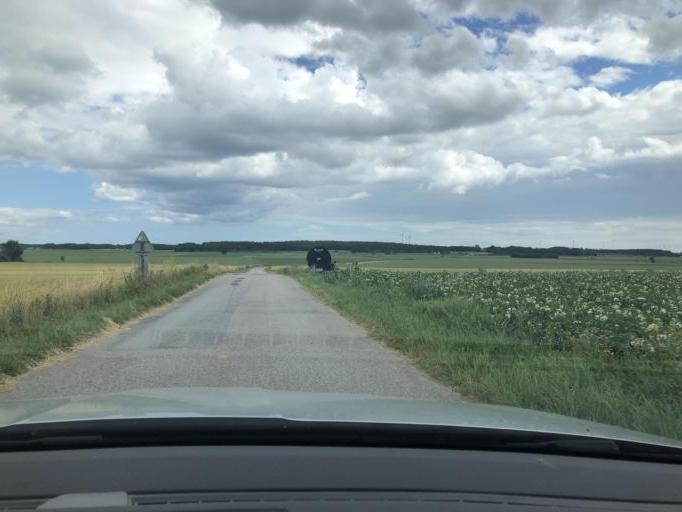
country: SE
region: Blekinge
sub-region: Solvesborgs Kommun
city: Soelvesborg
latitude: 56.1009
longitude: 14.6208
